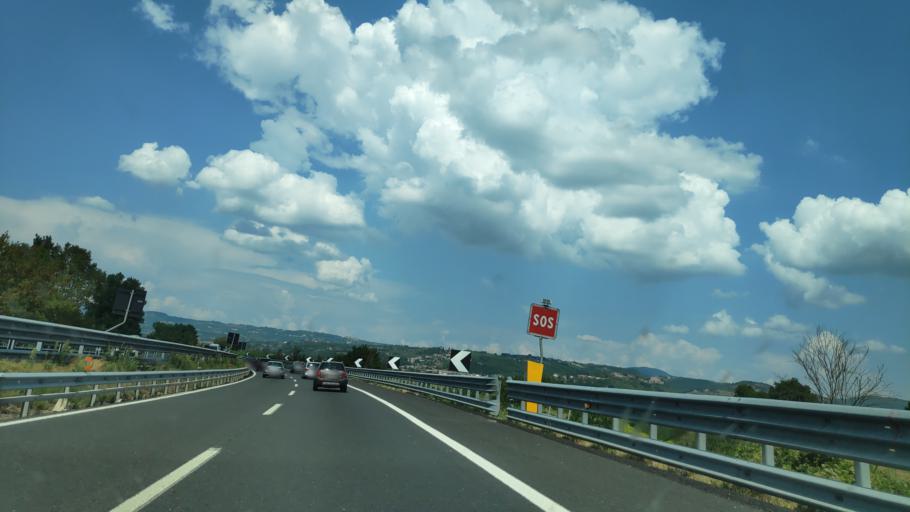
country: IT
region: Umbria
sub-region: Provincia di Terni
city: Fabro Scalo
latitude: 42.8577
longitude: 12.0384
